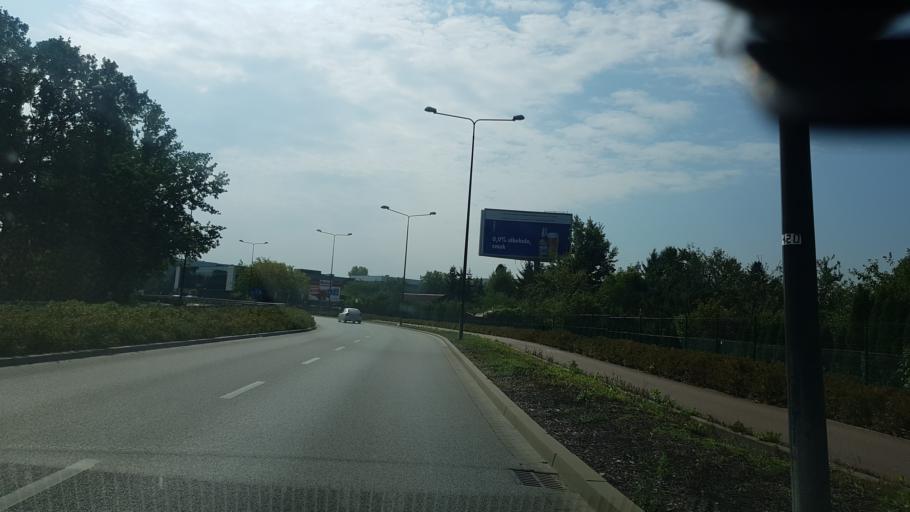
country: PL
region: Masovian Voivodeship
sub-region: Warszawa
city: Ursynow
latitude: 52.1665
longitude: 21.0448
